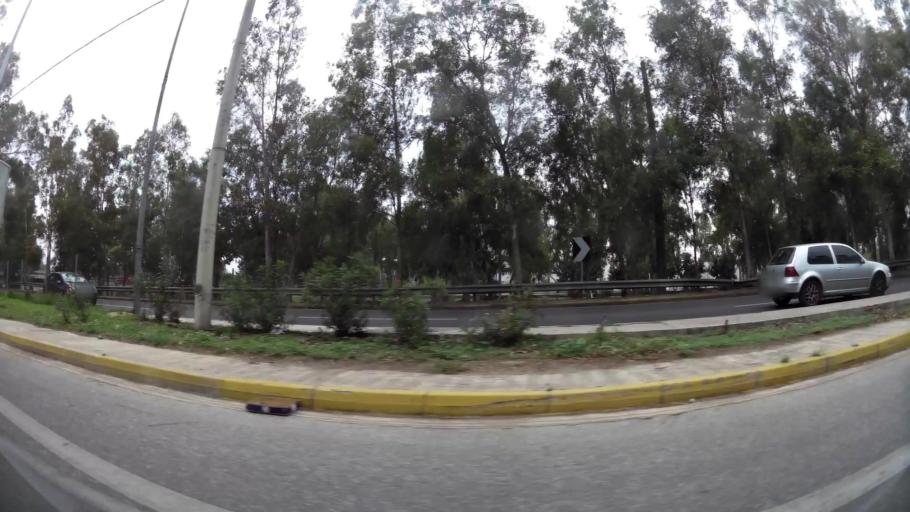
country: GR
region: Attica
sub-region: Nomarchia Athinas
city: Kallithea
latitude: 37.9395
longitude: 23.6951
